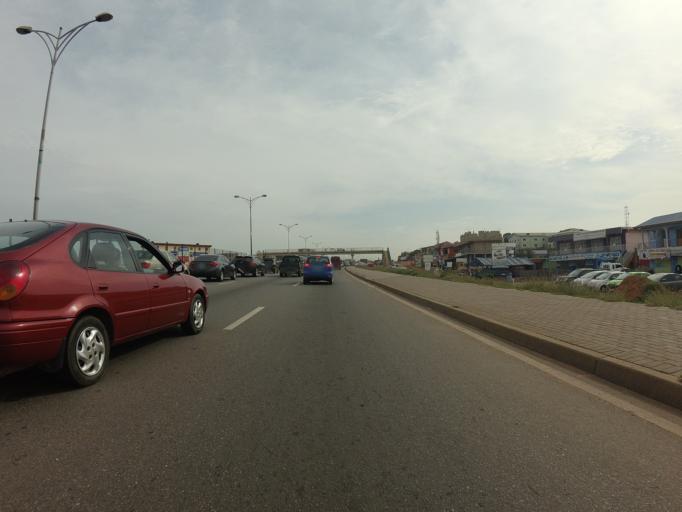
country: GH
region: Greater Accra
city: Gbawe
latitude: 5.6000
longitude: -0.2621
